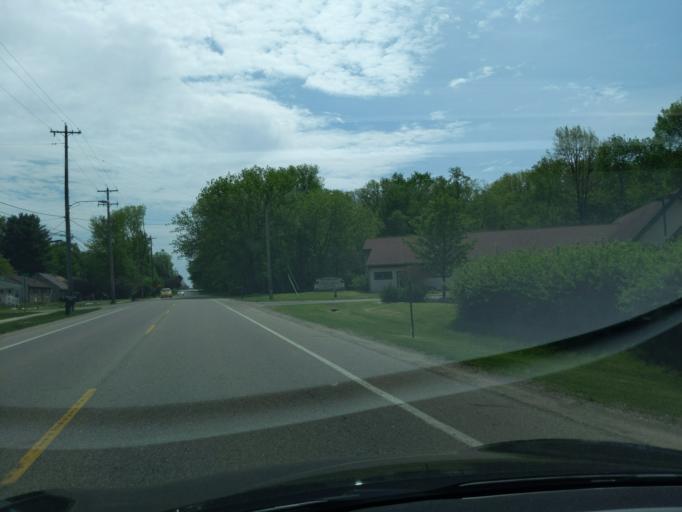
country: US
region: Michigan
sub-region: Ingham County
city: Holt
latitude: 42.6548
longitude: -84.5617
